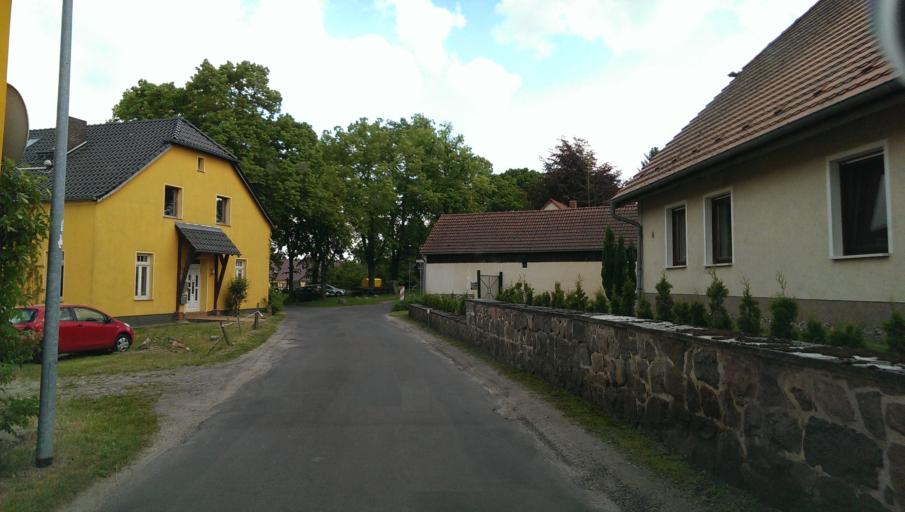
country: DE
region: Brandenburg
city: Wiesenburg
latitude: 52.1397
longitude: 12.5191
